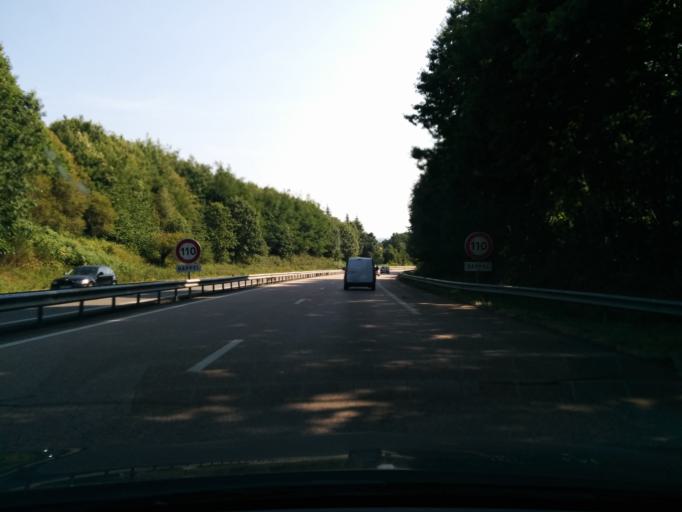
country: FR
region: Limousin
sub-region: Departement de la Haute-Vienne
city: Bonnac-la-Cote
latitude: 45.9501
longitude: 1.3152
